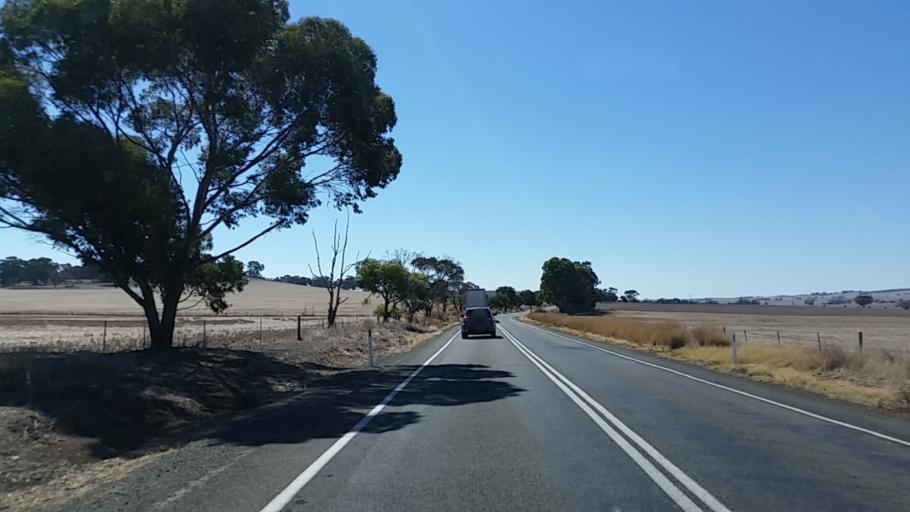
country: AU
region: South Australia
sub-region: Clare and Gilbert Valleys
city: Clare
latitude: -34.0307
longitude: 138.8027
